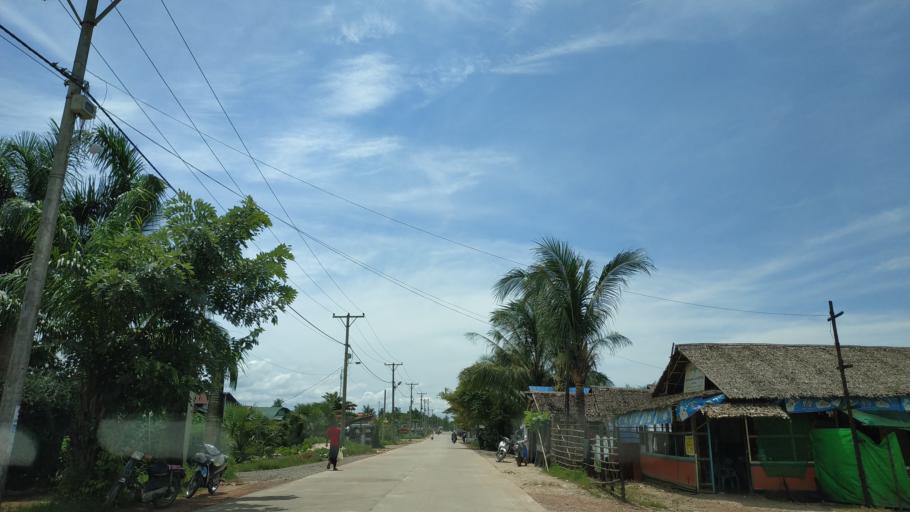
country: MM
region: Tanintharyi
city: Dawei
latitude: 14.0781
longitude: 98.1827
